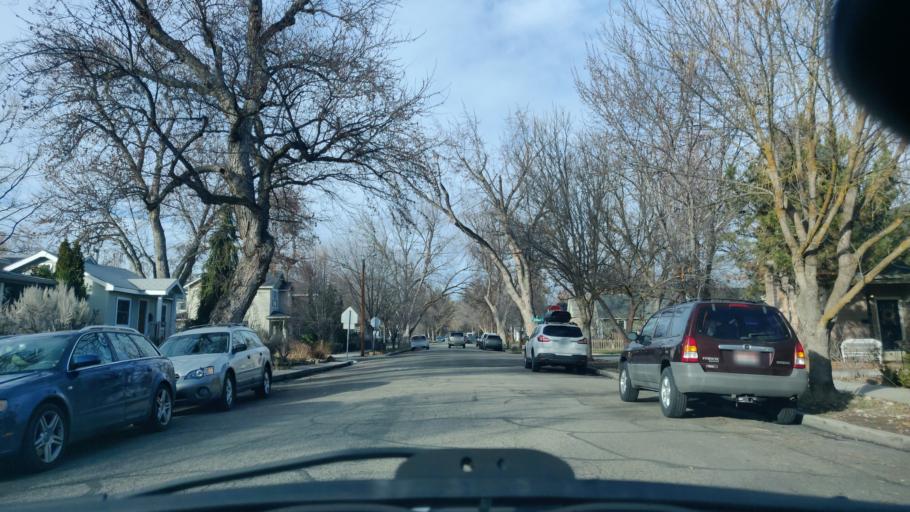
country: US
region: Idaho
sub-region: Ada County
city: Boise
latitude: 43.6288
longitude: -116.1999
